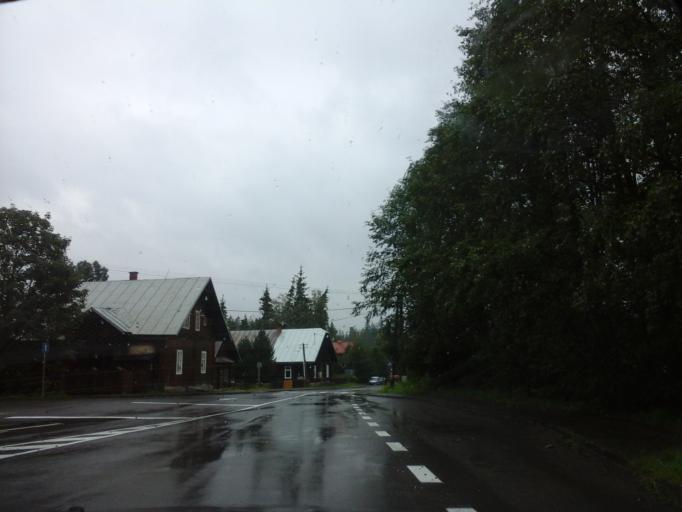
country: SK
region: Presovsky
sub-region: Okres Poprad
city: Zdiar
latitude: 49.2805
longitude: 20.1756
